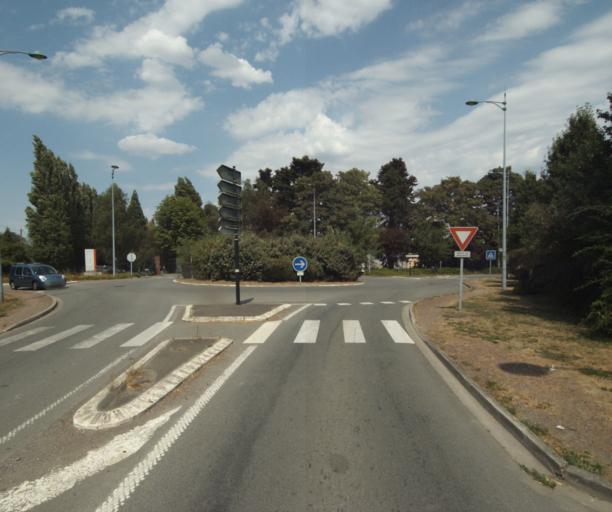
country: FR
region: Nord-Pas-de-Calais
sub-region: Departement du Nord
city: Wervicq-Sud
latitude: 50.7669
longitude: 3.0303
